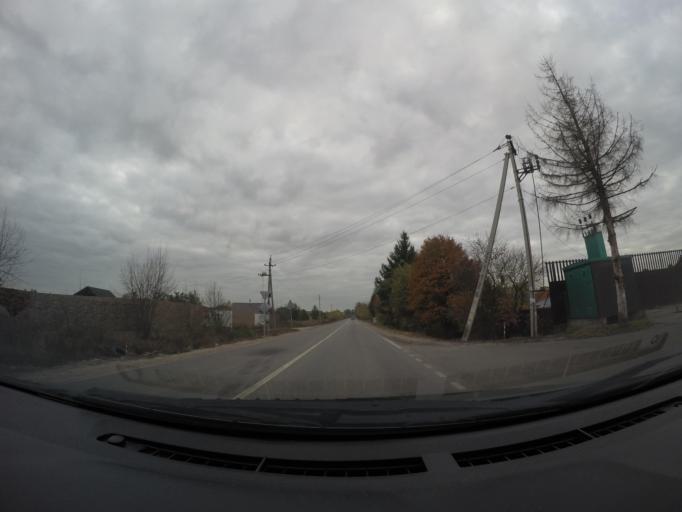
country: RU
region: Moskovskaya
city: Gzhel'
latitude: 55.6443
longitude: 38.3729
